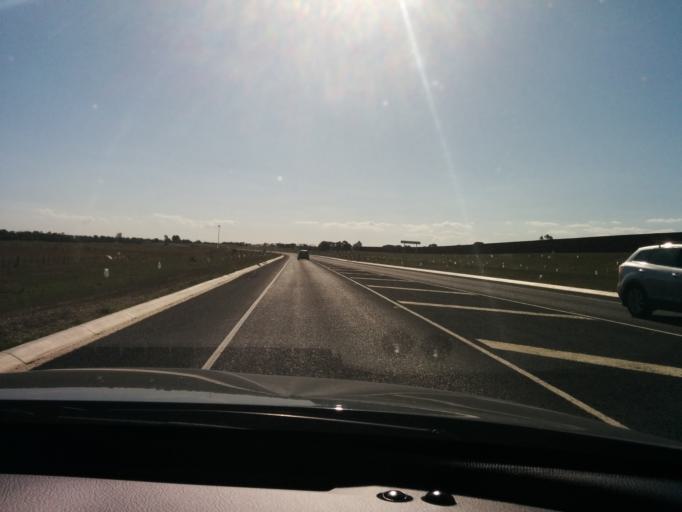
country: AU
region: Victoria
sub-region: Greater Geelong
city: Wandana Heights
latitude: -38.2150
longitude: 144.3241
